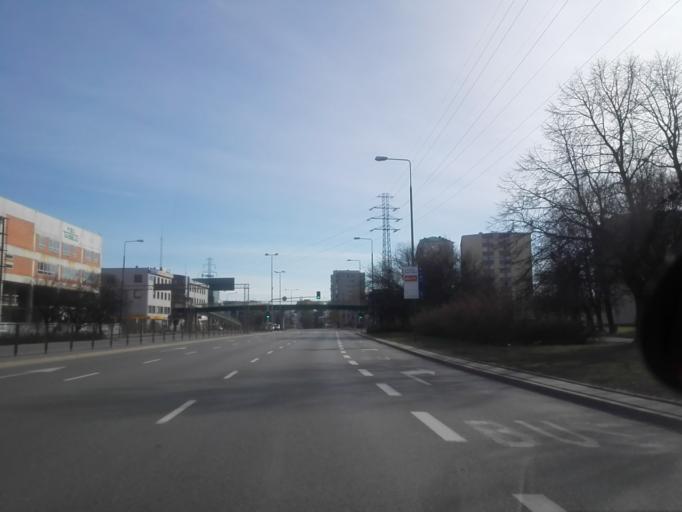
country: PL
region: Masovian Voivodeship
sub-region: Warszawa
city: Mokotow
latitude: 52.1762
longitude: 21.0023
